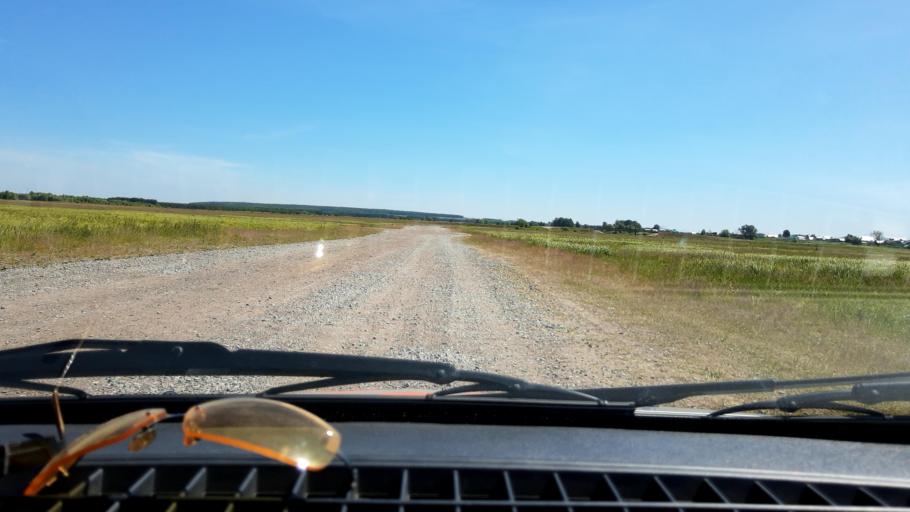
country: RU
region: Bashkortostan
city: Mikhaylovka
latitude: 54.9700
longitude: 55.7952
